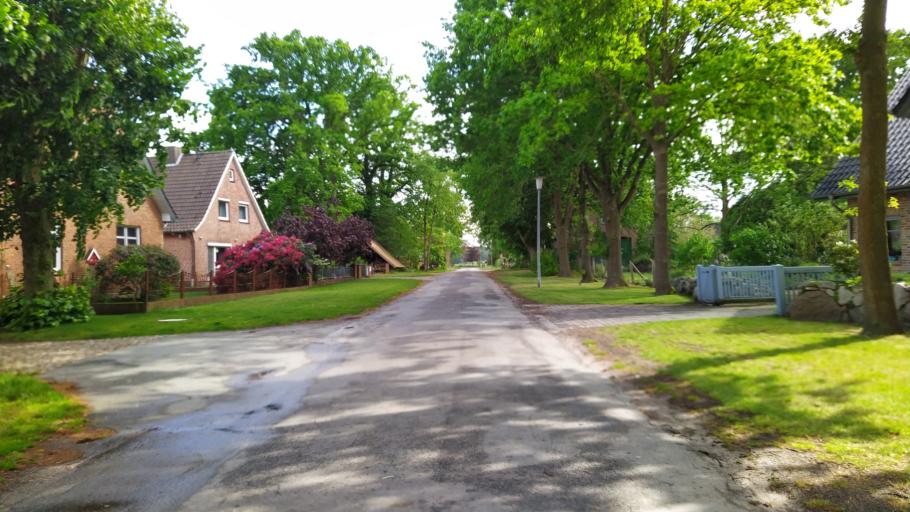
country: DE
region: Lower Saxony
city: Brest
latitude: 53.4506
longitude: 9.3866
